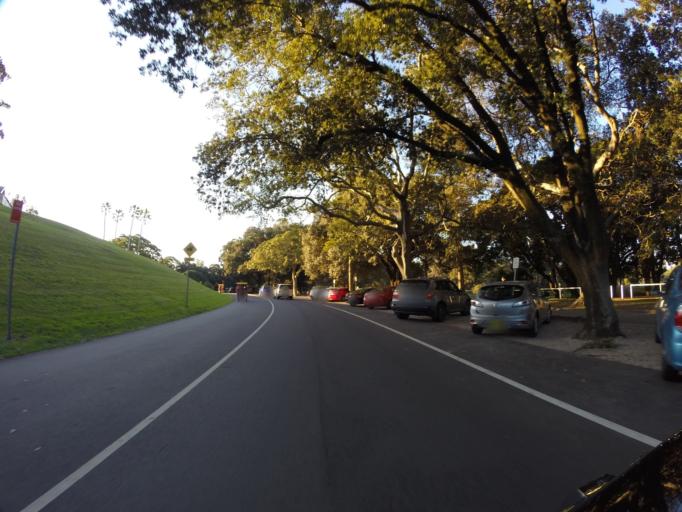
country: AU
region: New South Wales
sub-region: Woollahra
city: Woollahra
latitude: -33.8986
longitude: 151.2279
